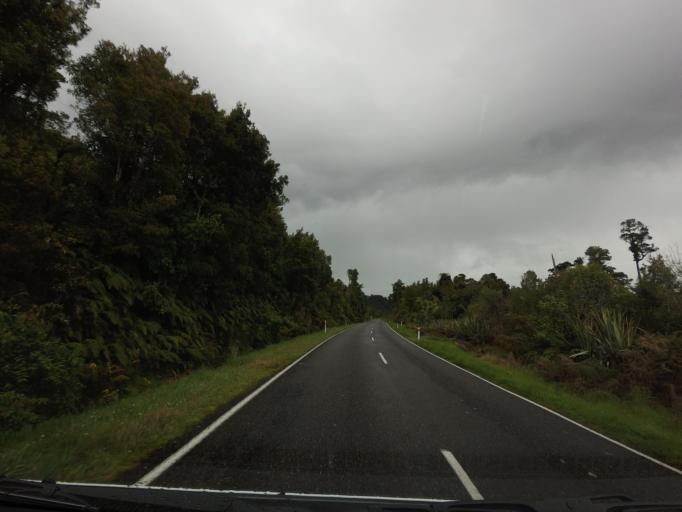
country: NZ
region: West Coast
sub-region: Westland District
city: Hokitika
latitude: -43.0514
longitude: 170.6378
